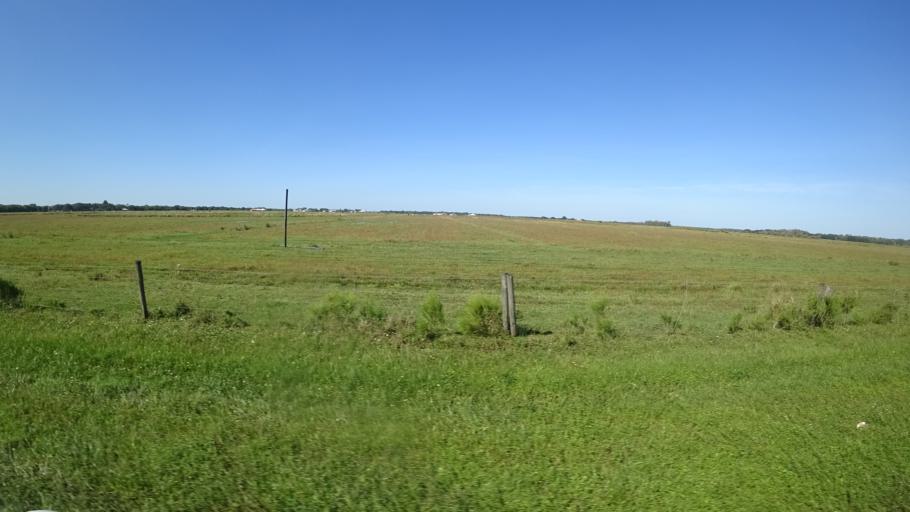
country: US
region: Florida
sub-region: Sarasota County
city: Lake Sarasota
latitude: 27.3408
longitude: -82.2693
